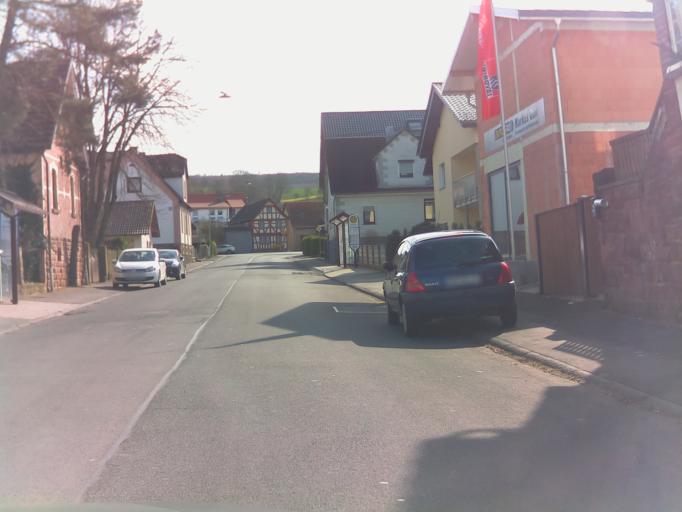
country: DE
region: Hesse
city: Budingen
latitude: 50.2879
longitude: 9.0684
